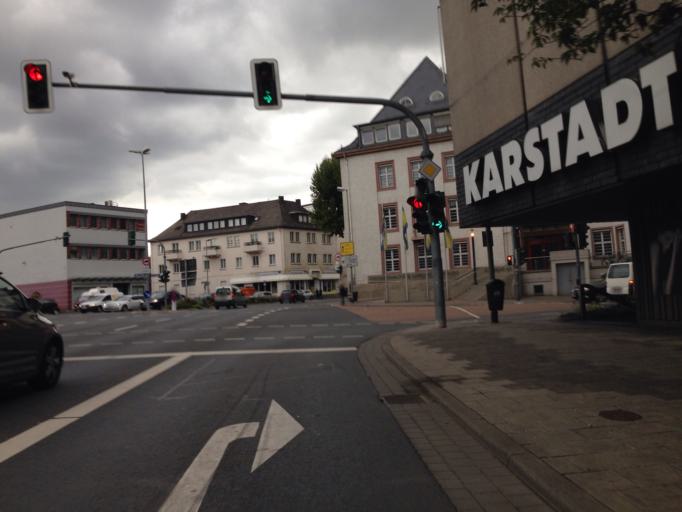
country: DE
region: Hesse
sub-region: Regierungsbezirk Giessen
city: Limburg an der Lahn
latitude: 50.3865
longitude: 8.0596
